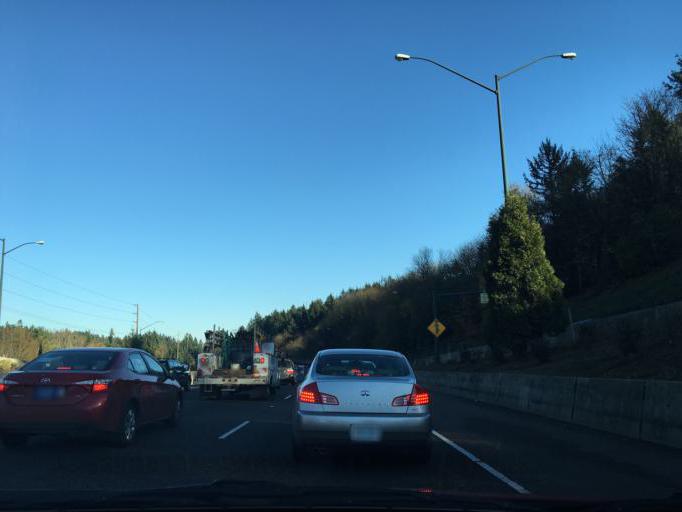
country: US
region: Oregon
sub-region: Washington County
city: West Slope
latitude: 45.5086
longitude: -122.7349
